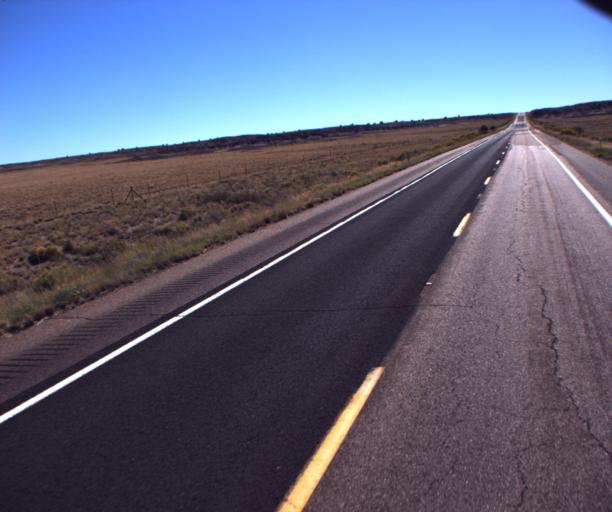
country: US
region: Arizona
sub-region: Navajo County
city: Snowflake
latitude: 34.7236
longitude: -109.7755
